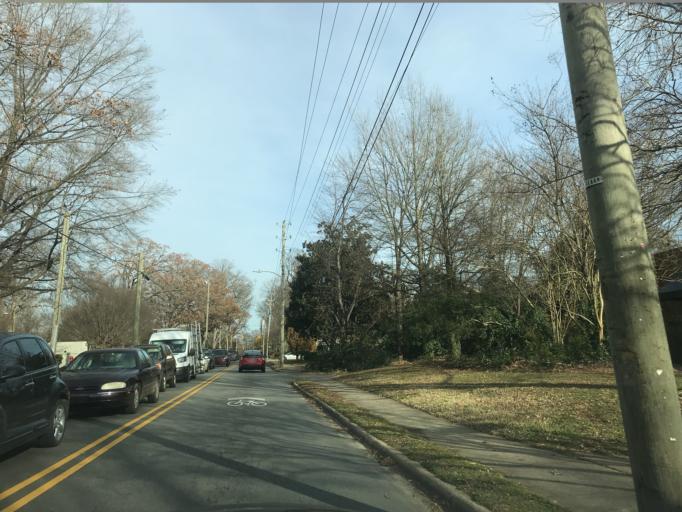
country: US
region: North Carolina
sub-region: Wake County
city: West Raleigh
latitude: 35.8044
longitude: -78.6449
